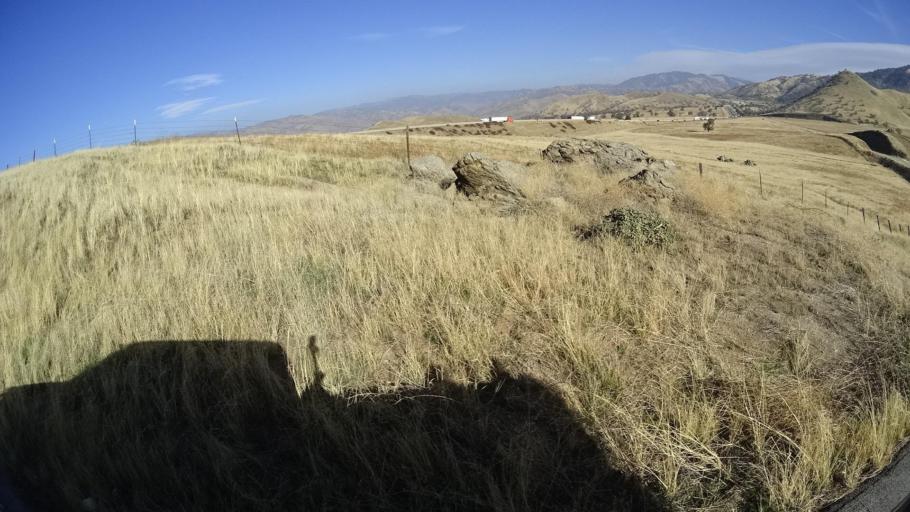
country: US
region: California
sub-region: Kern County
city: Bear Valley Springs
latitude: 35.2656
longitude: -118.6720
